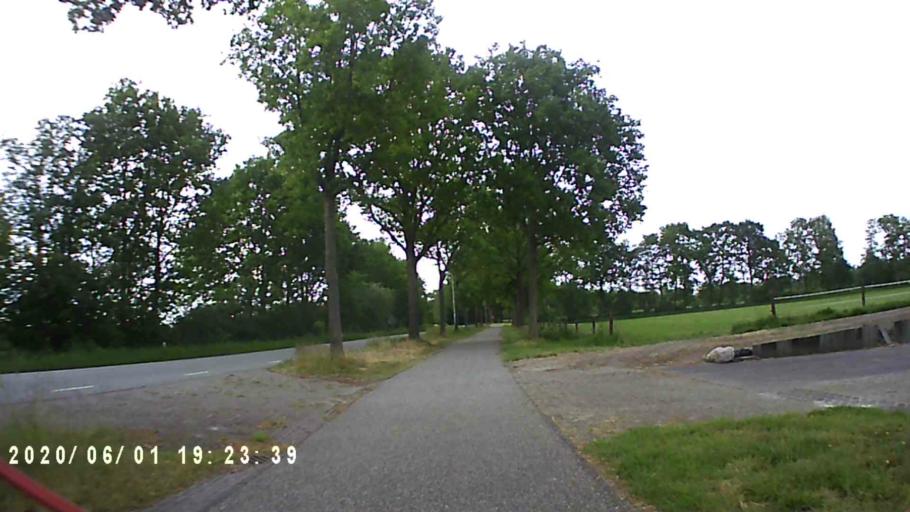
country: NL
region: Friesland
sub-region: Gemeente Achtkarspelen
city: Drogeham
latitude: 53.2037
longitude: 6.1270
